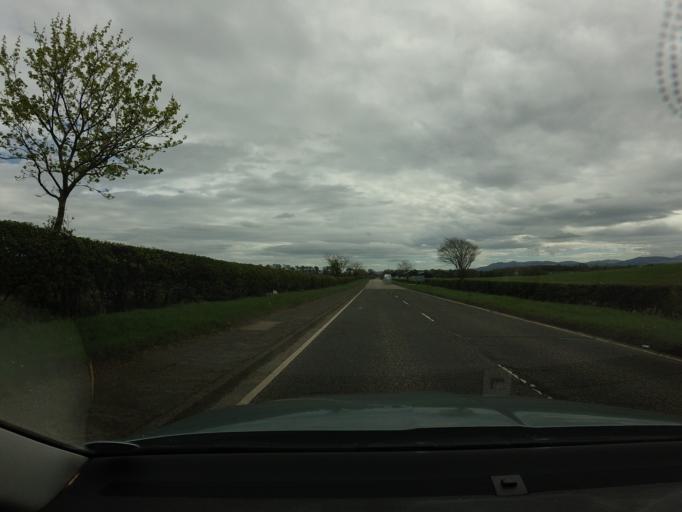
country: GB
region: Scotland
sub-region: Edinburgh
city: Kirkliston
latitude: 55.9609
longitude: -3.4366
